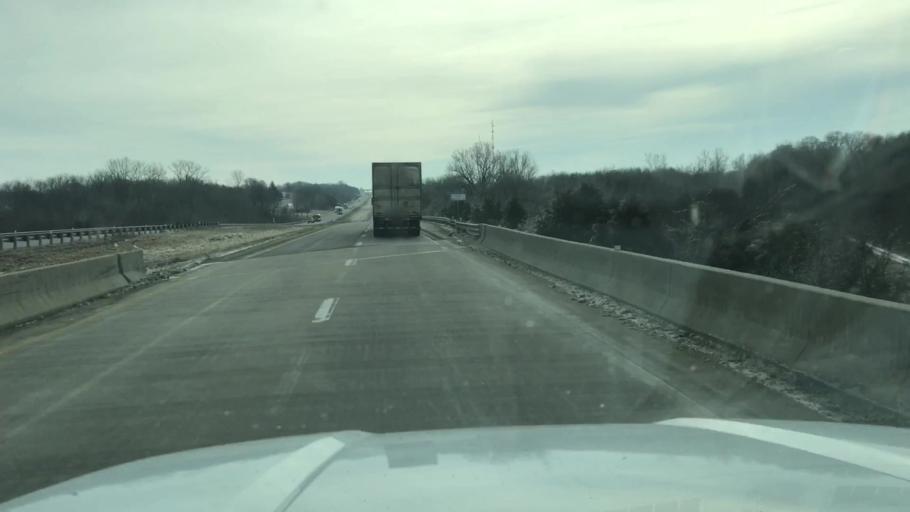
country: US
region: Missouri
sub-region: Andrew County
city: Country Club Village
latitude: 39.8709
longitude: -94.8317
